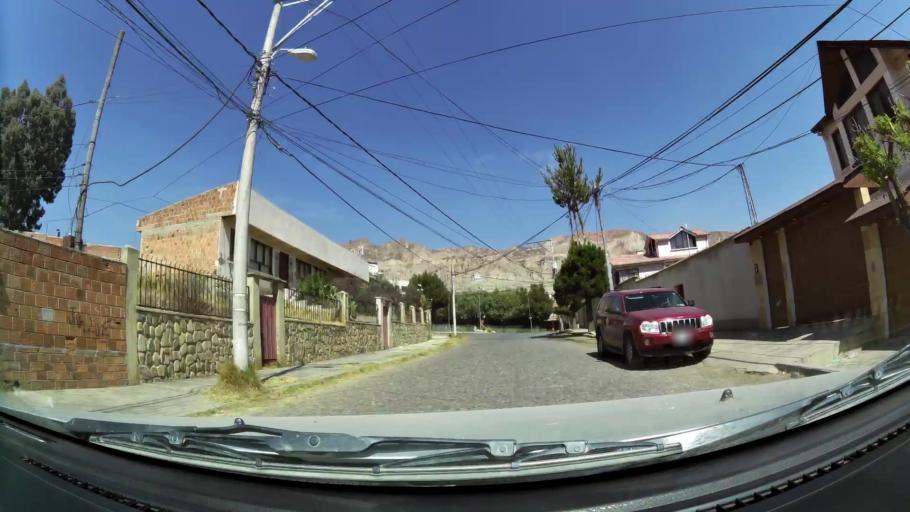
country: BO
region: La Paz
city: La Paz
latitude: -16.5431
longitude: -68.0673
